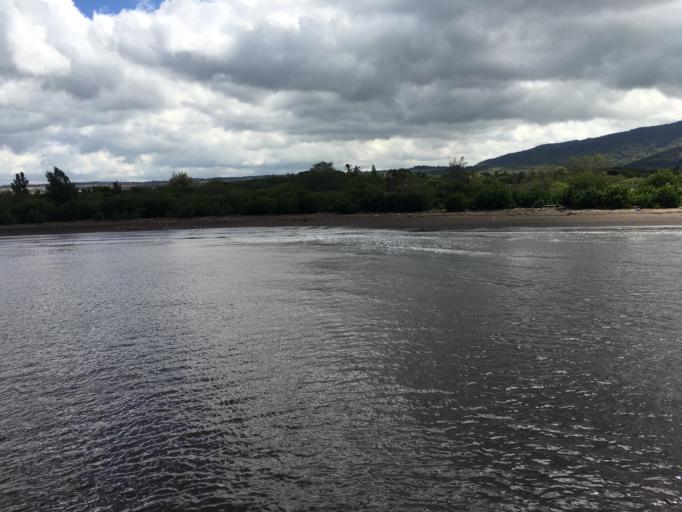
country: US
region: Hawaii
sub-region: Honolulu County
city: Hale'iwa
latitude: 21.5808
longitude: -158.1197
